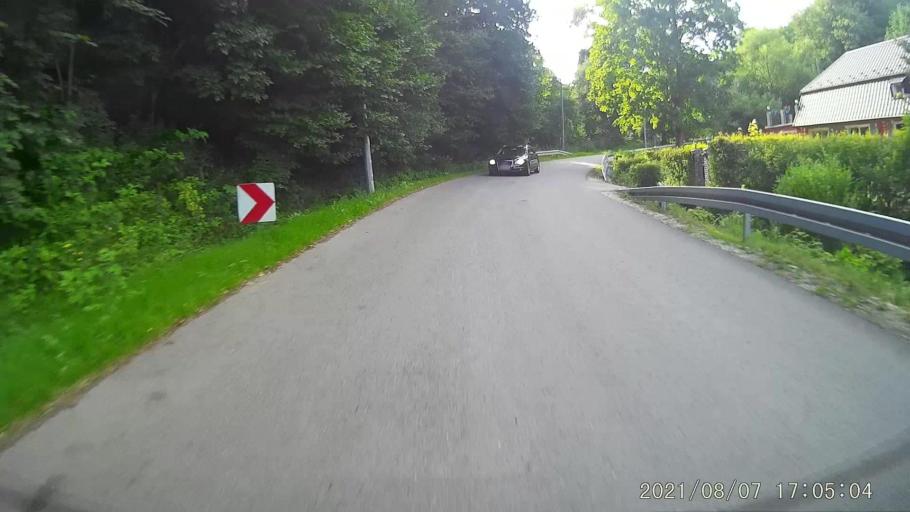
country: PL
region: Lower Silesian Voivodeship
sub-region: Powiat klodzki
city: Bystrzyca Klodzka
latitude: 50.2938
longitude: 16.5748
